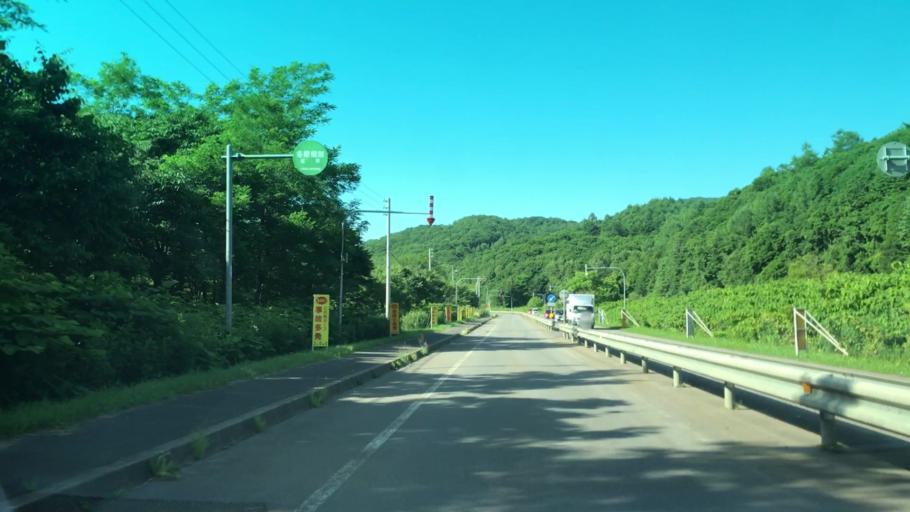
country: JP
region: Hokkaido
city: Iwanai
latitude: 42.9983
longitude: 140.6679
